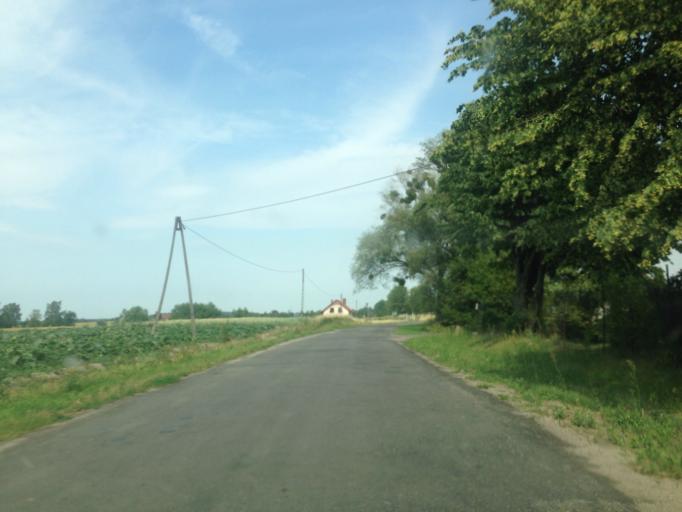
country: PL
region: Kujawsko-Pomorskie
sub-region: Powiat brodnicki
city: Bobrowo
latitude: 53.2839
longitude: 19.3286
